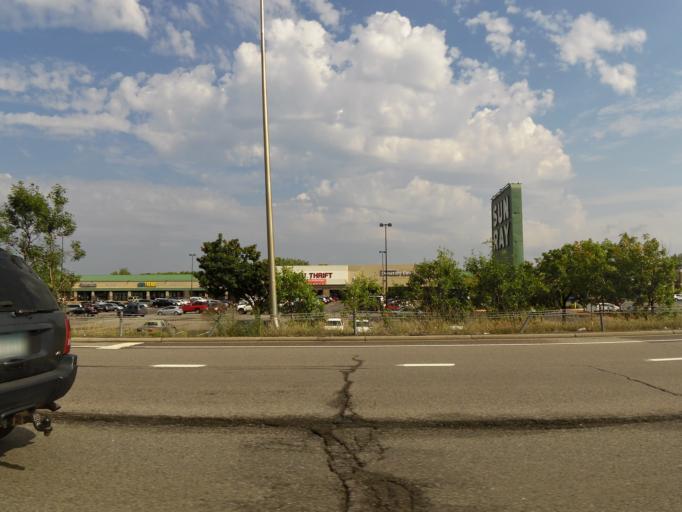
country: US
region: Minnesota
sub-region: Ramsey County
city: Maplewood
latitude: 44.9509
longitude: -93.0095
